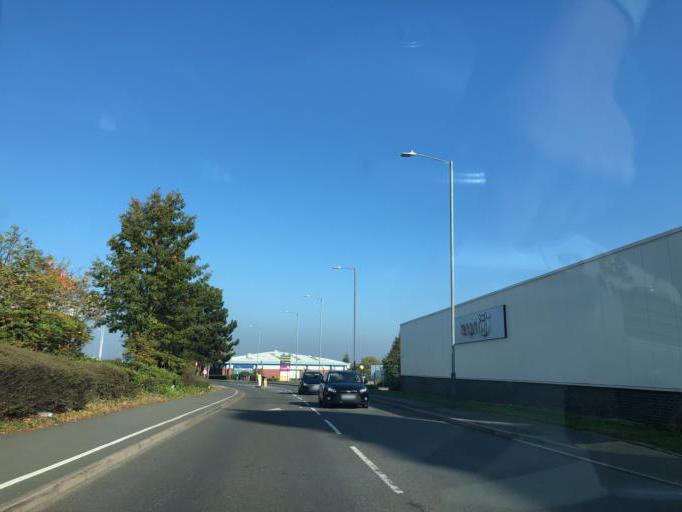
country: GB
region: England
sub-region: Warwickshire
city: Royal Leamington Spa
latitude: 52.2785
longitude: -1.5456
